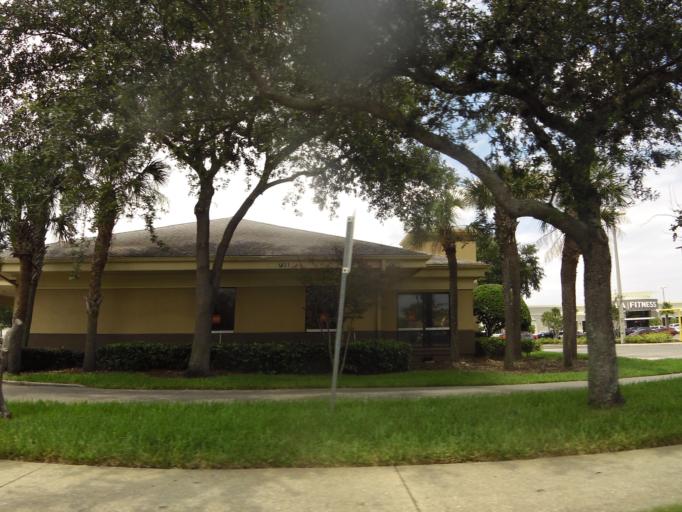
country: US
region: Florida
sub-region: Duval County
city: Atlantic Beach
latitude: 30.3246
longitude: -81.4126
